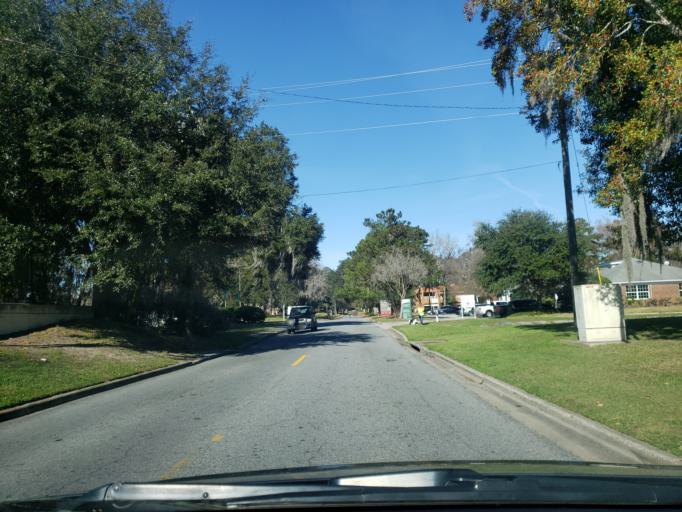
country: US
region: Georgia
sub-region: Chatham County
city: Montgomery
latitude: 31.9843
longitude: -81.1526
